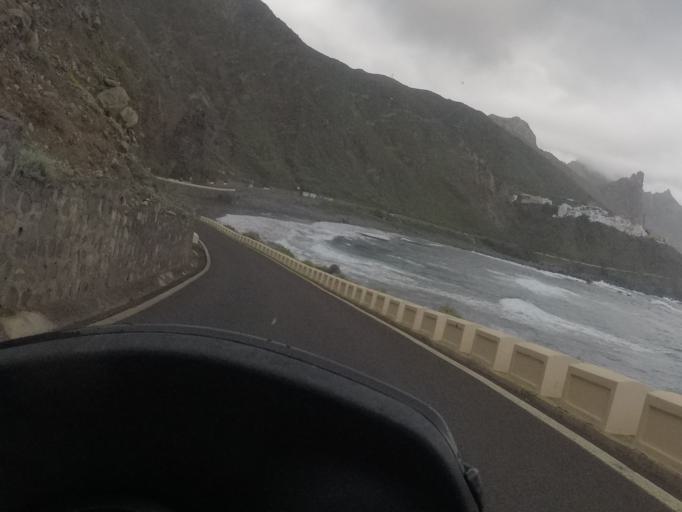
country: ES
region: Canary Islands
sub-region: Provincia de Santa Cruz de Tenerife
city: Santa Cruz de Tenerife
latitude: 28.5745
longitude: -16.1905
